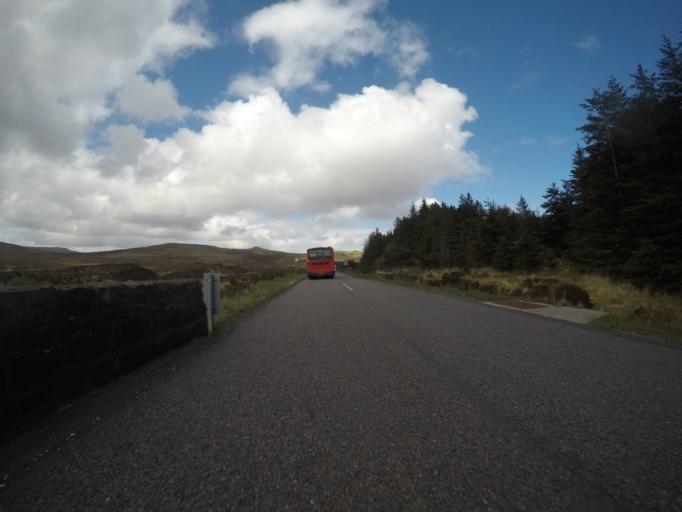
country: GB
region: Scotland
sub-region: Highland
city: Isle of Skye
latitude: 57.3192
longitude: -6.2037
